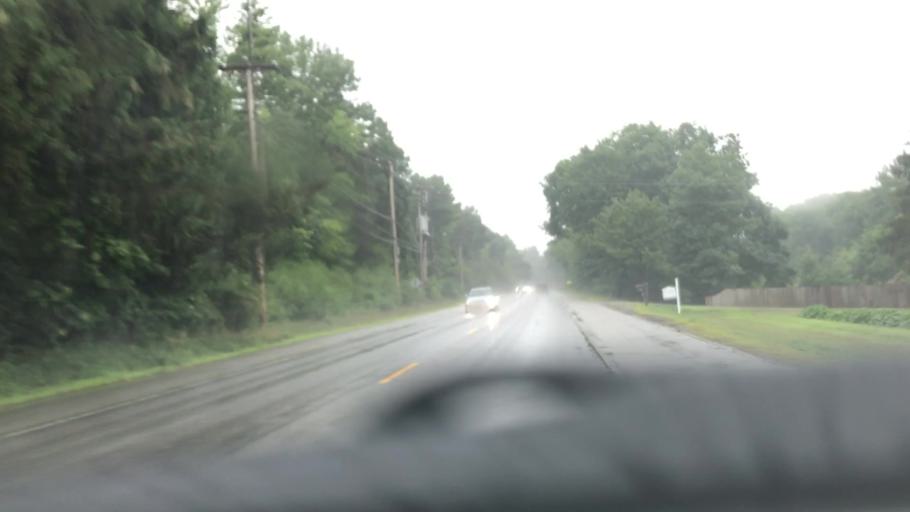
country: US
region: Maine
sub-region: York County
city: North Berwick
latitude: 43.3069
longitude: -70.6749
